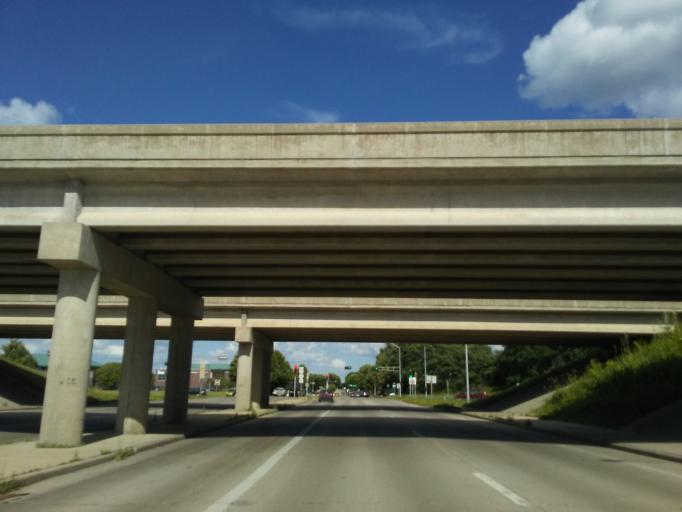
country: US
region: Wisconsin
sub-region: Dane County
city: Middleton
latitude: 43.0749
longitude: -89.5223
